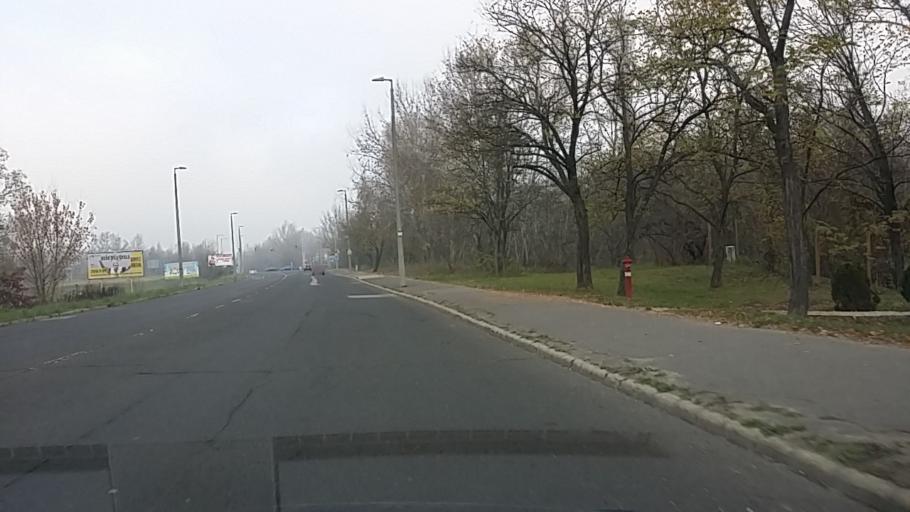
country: HU
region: Budapest
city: Budapest XV. keruelet
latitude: 47.5881
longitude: 19.1028
